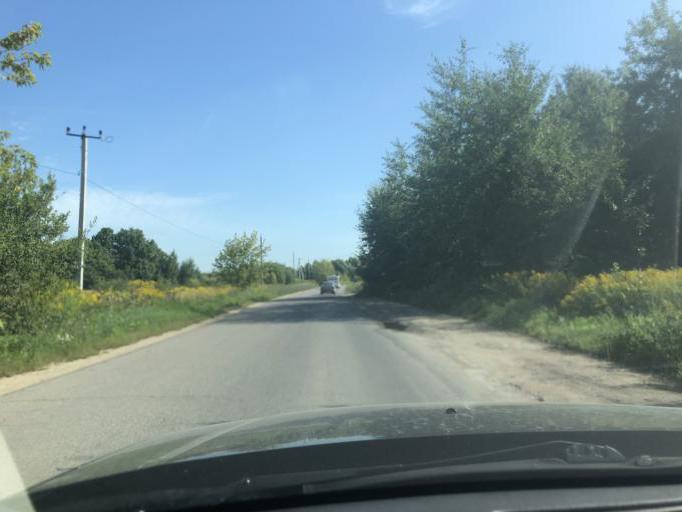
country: RU
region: Tula
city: Mendeleyevskiy
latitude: 54.1274
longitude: 37.6095
